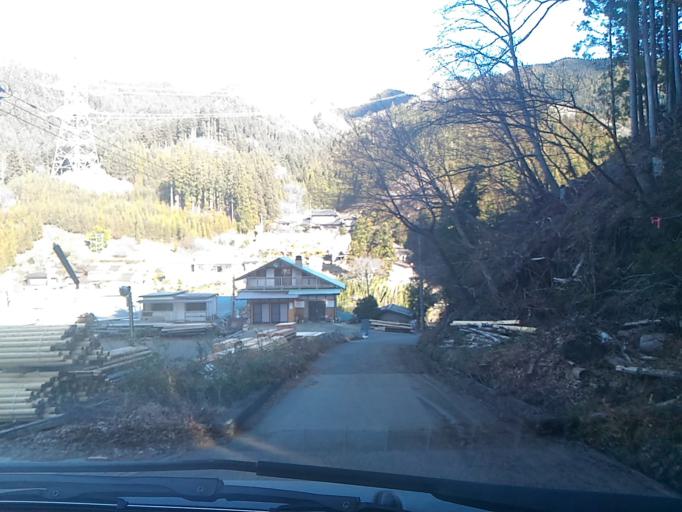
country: JP
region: Fukushima
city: Ishikawa
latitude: 37.0517
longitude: 140.6064
